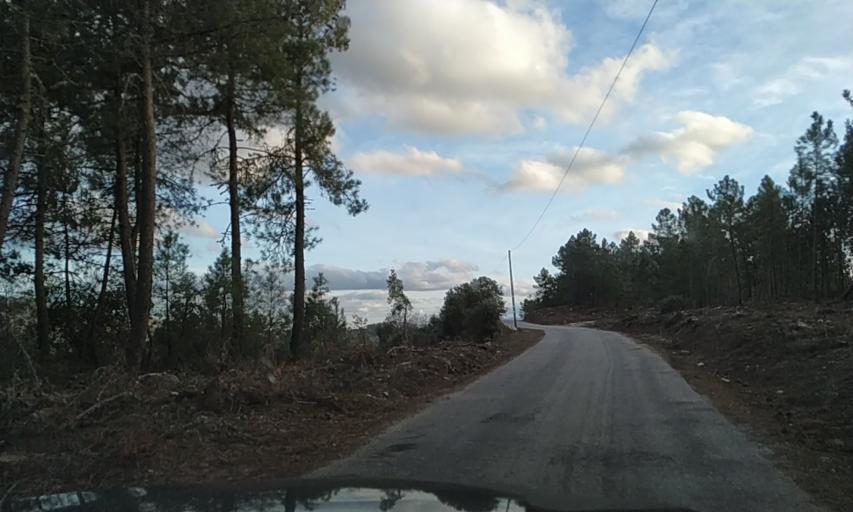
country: PT
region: Braganca
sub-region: Carrazeda de Ansiaes
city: Carrazeda de Anciaes
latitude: 41.2142
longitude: -7.3635
